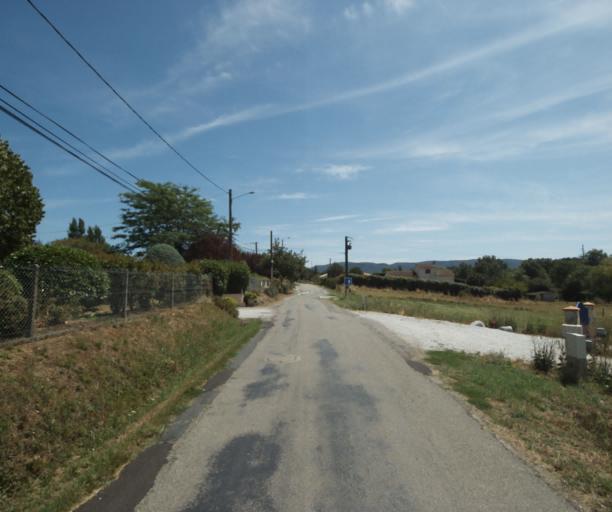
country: FR
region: Midi-Pyrenees
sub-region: Departement de la Haute-Garonne
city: Revel
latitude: 43.4887
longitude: 2.0251
